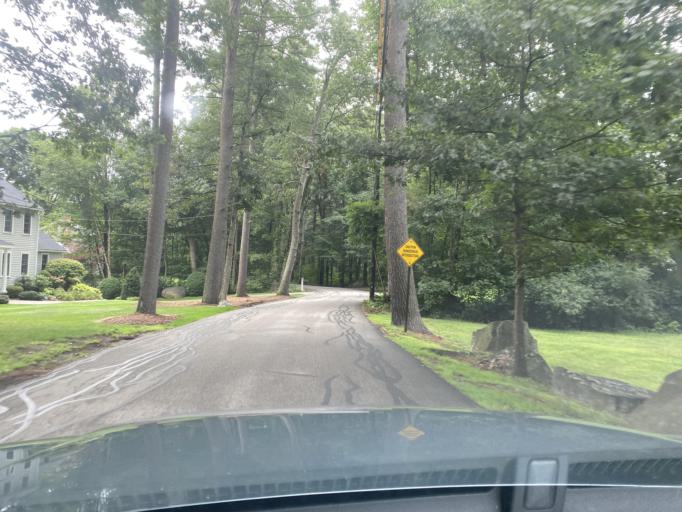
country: US
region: Massachusetts
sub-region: Worcester County
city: Milford
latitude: 42.1396
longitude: -71.4632
